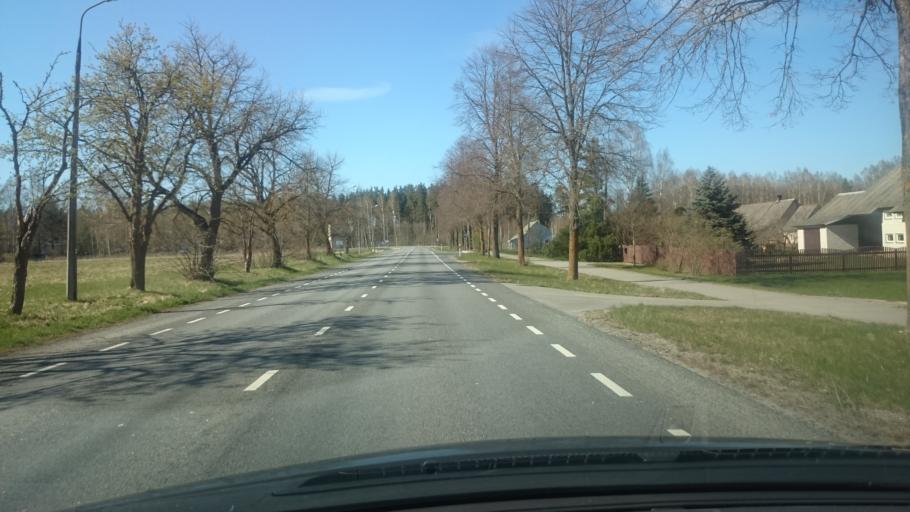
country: EE
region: Polvamaa
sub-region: Polva linn
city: Polva
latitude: 58.2151
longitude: 27.0701
